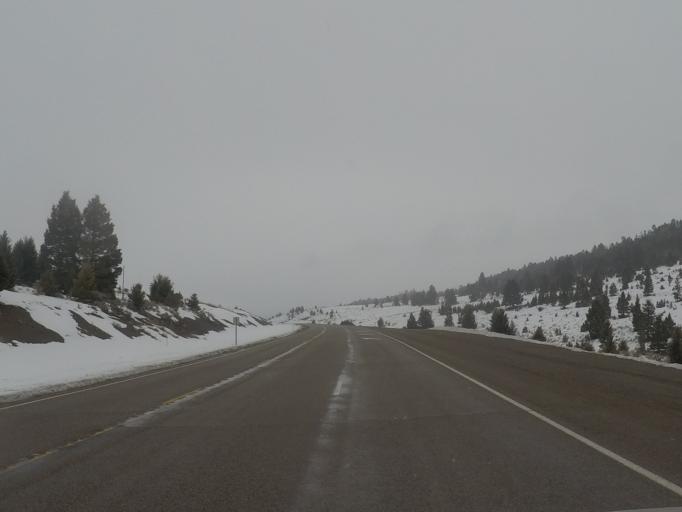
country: US
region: Montana
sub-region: Meagher County
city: White Sulphur Springs
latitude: 46.6506
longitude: -110.8707
